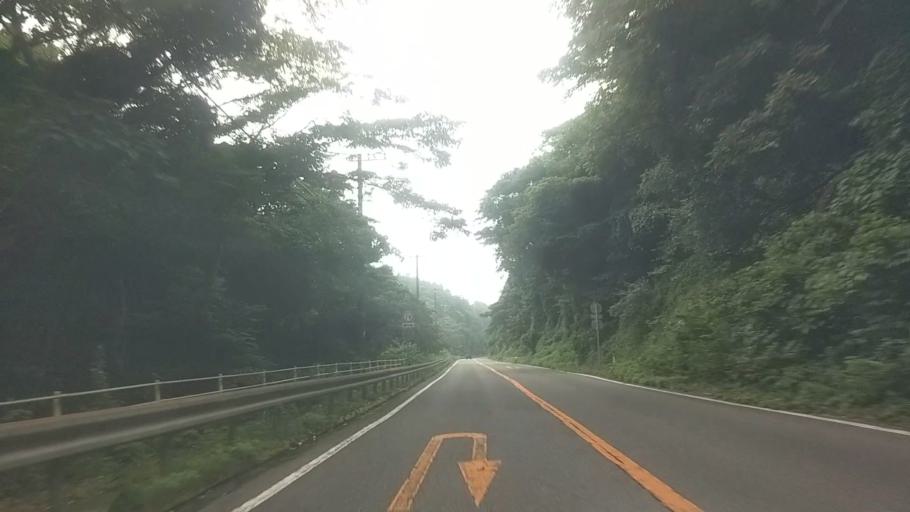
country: JP
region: Chiba
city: Katsuura
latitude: 35.1648
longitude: 140.3211
